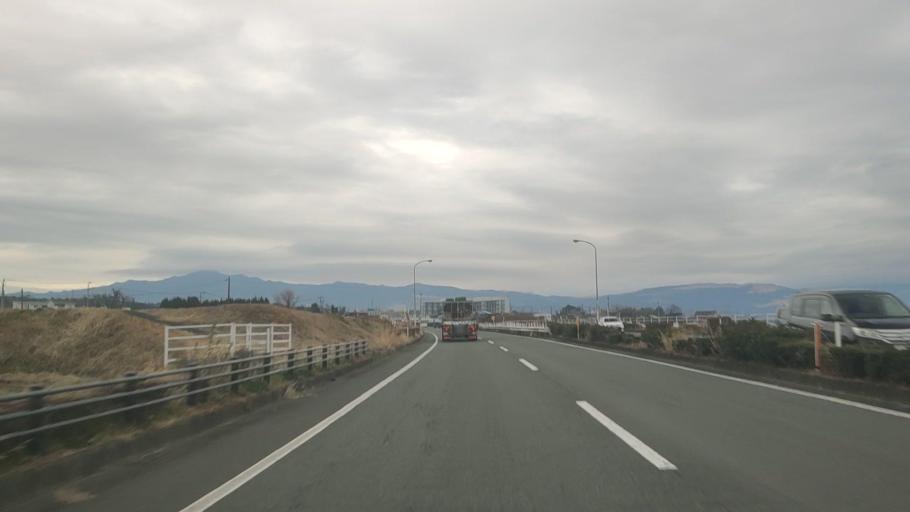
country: JP
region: Kumamoto
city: Ozu
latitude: 32.8697
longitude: 130.8416
